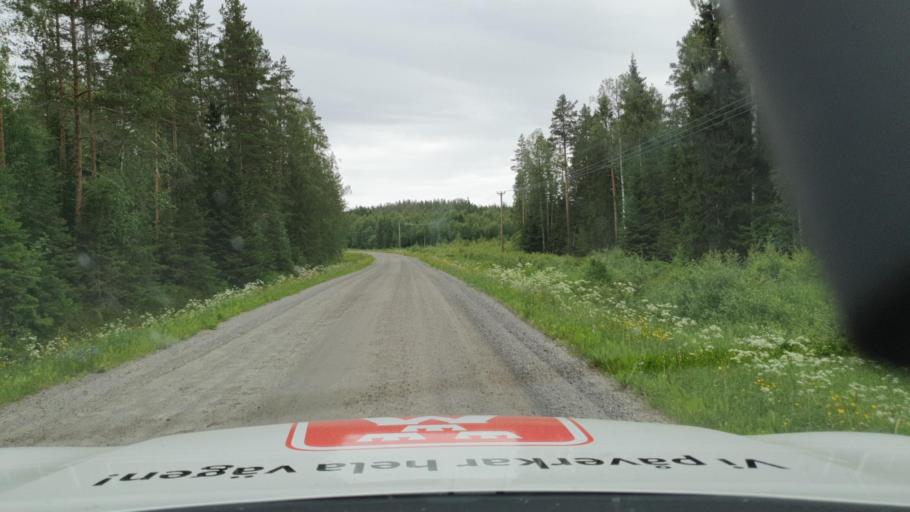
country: SE
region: Vaesterbotten
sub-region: Nordmalings Kommun
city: Nordmaling
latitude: 63.7362
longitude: 19.5036
